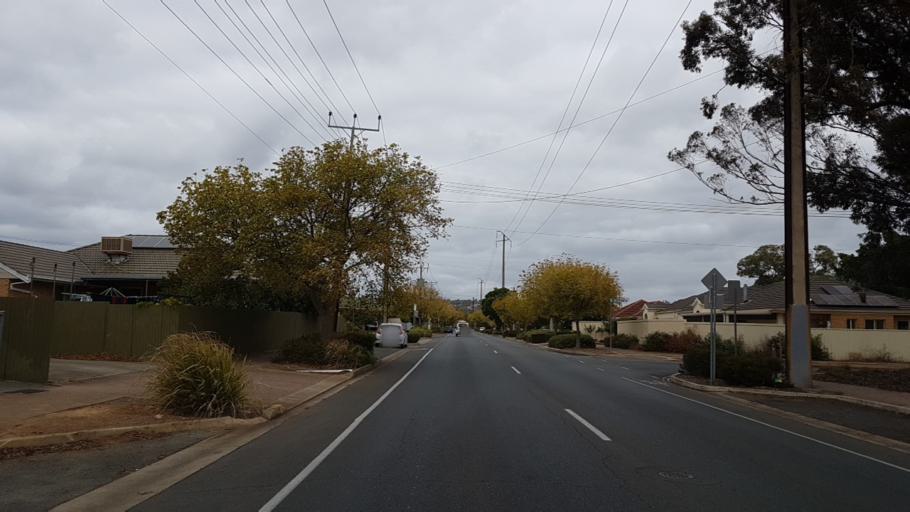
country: AU
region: South Australia
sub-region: Marion
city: Marion
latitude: -35.0089
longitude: 138.5660
